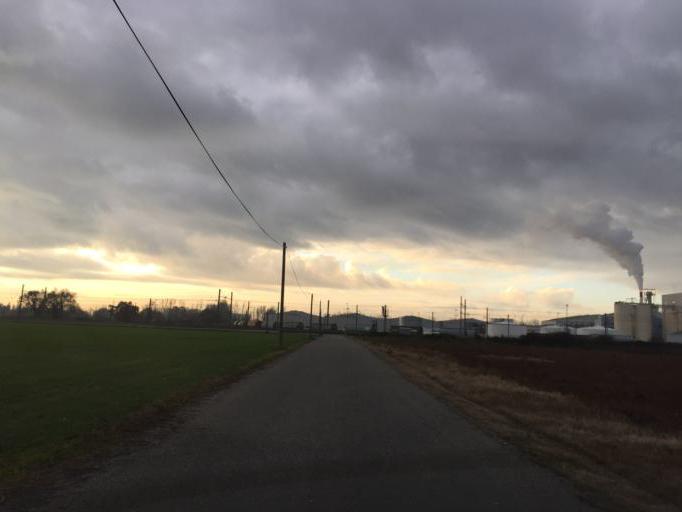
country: FR
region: Provence-Alpes-Cote d'Azur
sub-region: Departement du Vaucluse
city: Orange
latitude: 44.1329
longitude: 4.8471
